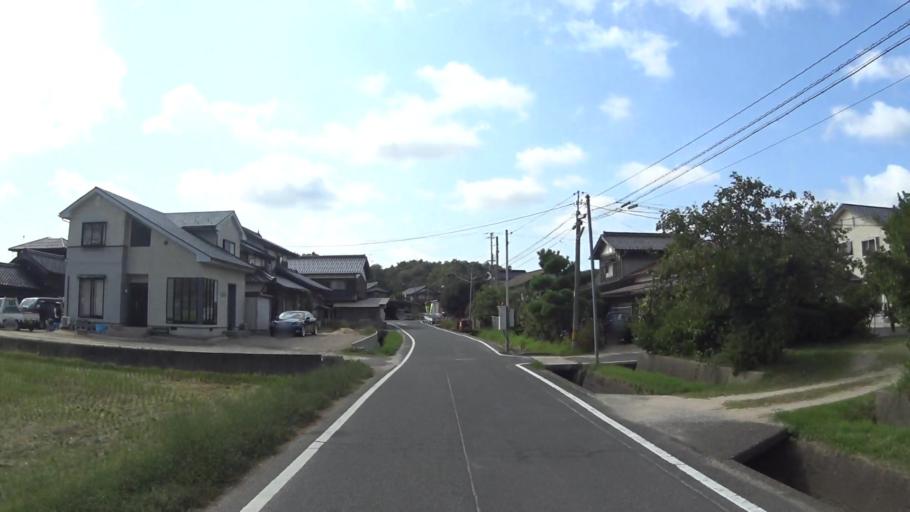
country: JP
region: Kyoto
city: Miyazu
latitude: 35.6547
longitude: 135.0934
